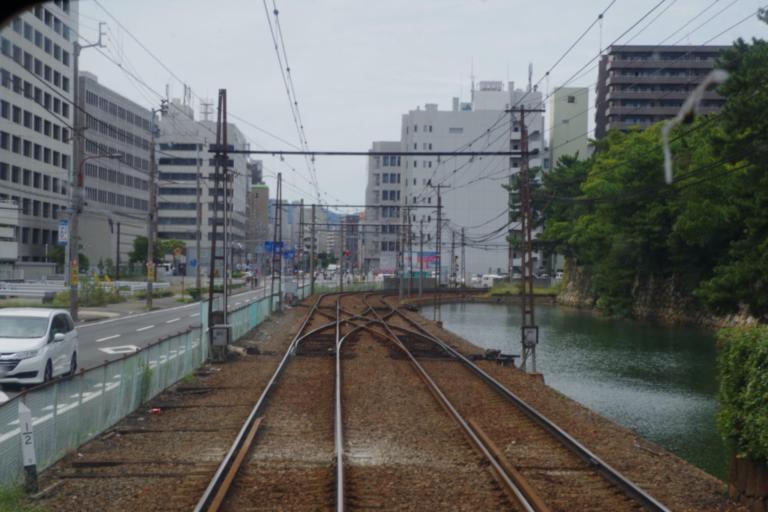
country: JP
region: Kagawa
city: Takamatsu-shi
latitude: 34.3485
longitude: 134.0521
